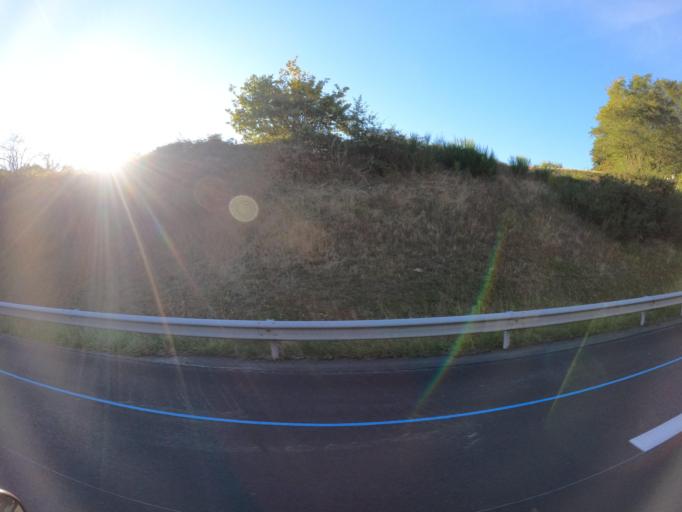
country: FR
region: Pays de la Loire
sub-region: Departement de la Vendee
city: Saint-Laurent-sur-Sevre
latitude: 46.9691
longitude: -0.9190
